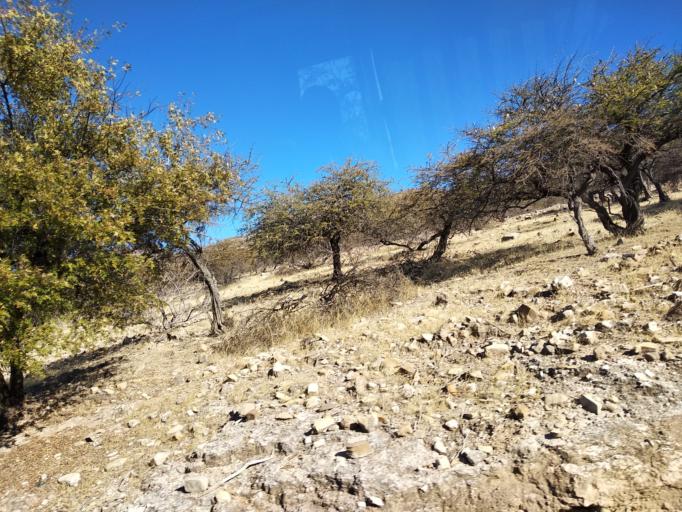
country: BO
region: Cochabamba
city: Mizque
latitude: -18.0828
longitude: -65.7477
